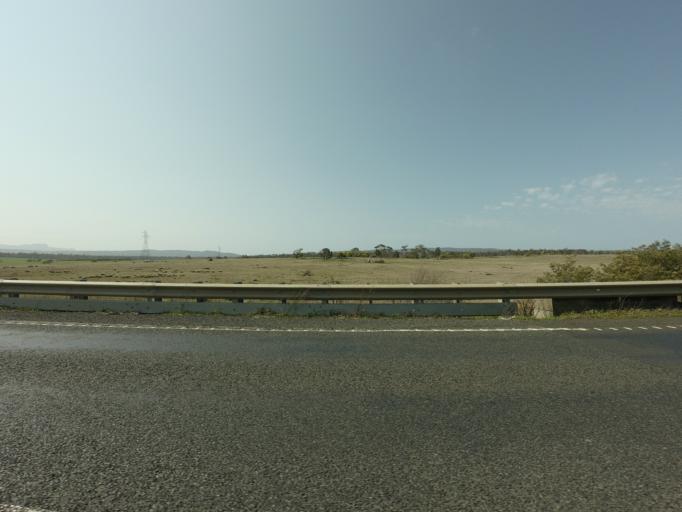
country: AU
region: Tasmania
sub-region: Northern Midlands
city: Evandale
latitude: -41.8393
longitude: 147.4482
